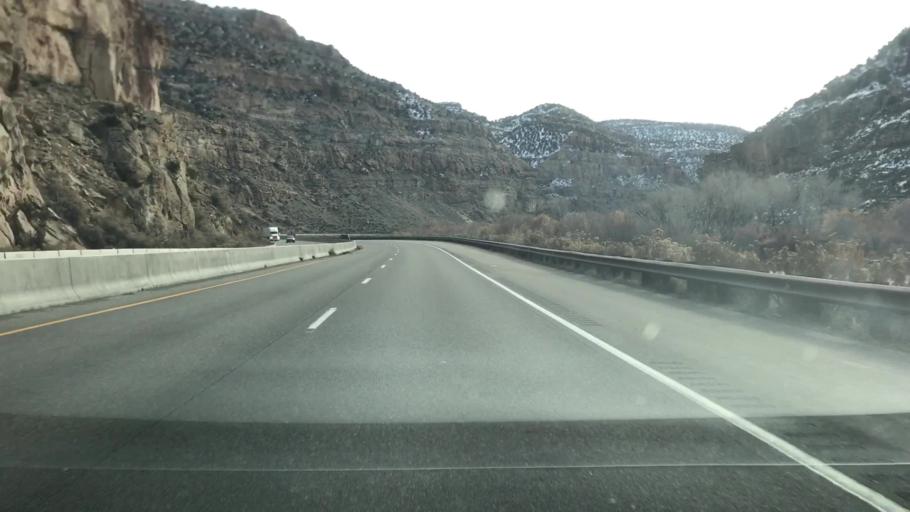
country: US
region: Colorado
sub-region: Mesa County
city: Palisade
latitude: 39.2290
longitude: -108.2644
